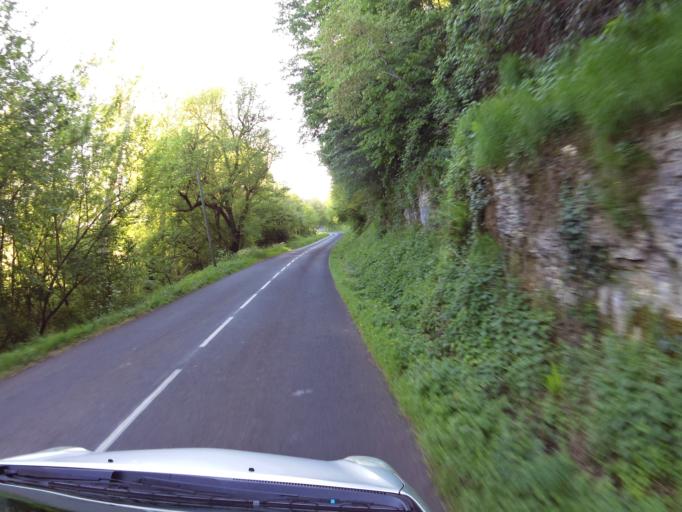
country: FR
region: Aquitaine
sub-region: Departement de la Dordogne
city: Carsac-Aillac
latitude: 44.8394
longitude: 1.3130
